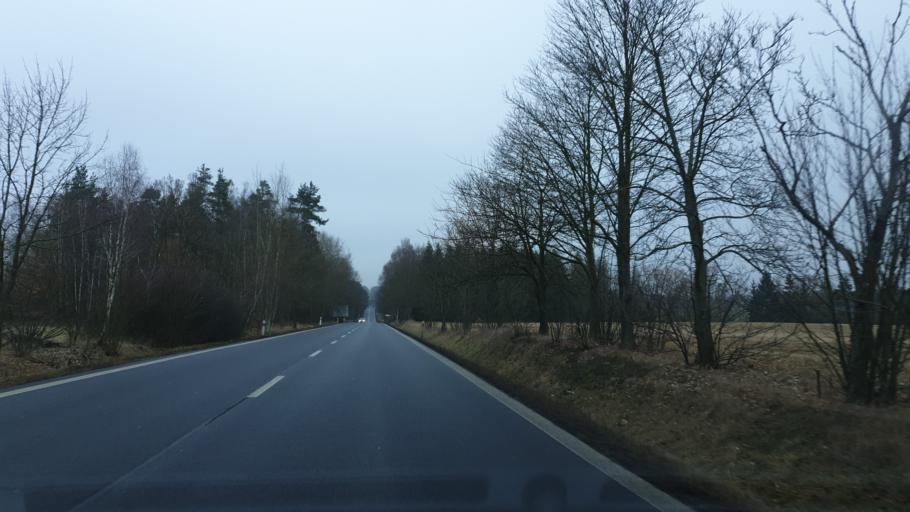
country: CZ
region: Karlovarsky
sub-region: Okres Cheb
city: Frantiskovy Lazne
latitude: 50.1360
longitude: 12.3380
